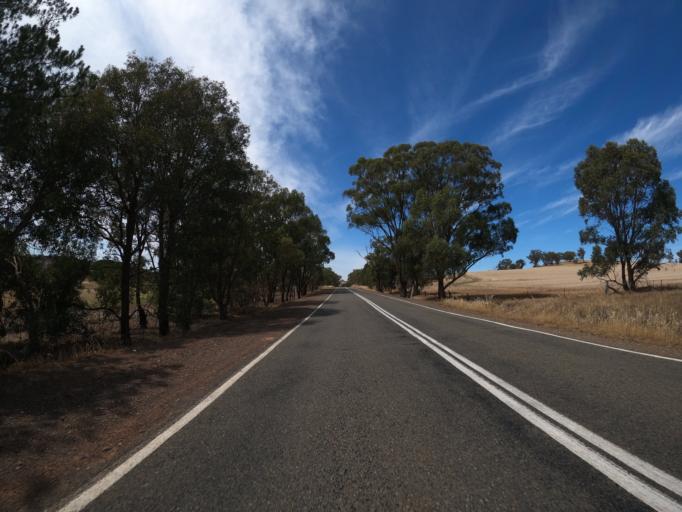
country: AU
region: Victoria
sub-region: Benalla
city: Benalla
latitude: -36.3240
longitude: 145.9591
